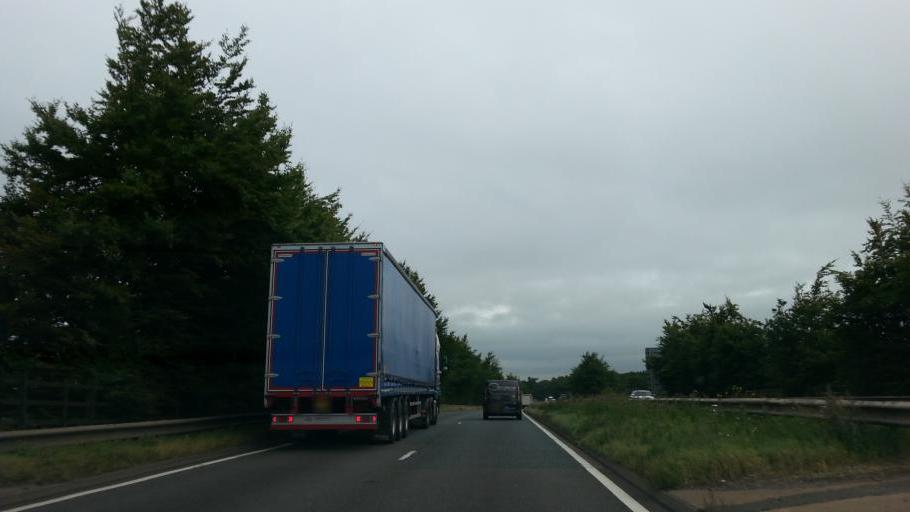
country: GB
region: England
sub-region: Nottinghamshire
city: Babworth
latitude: 53.3031
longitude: -1.0317
